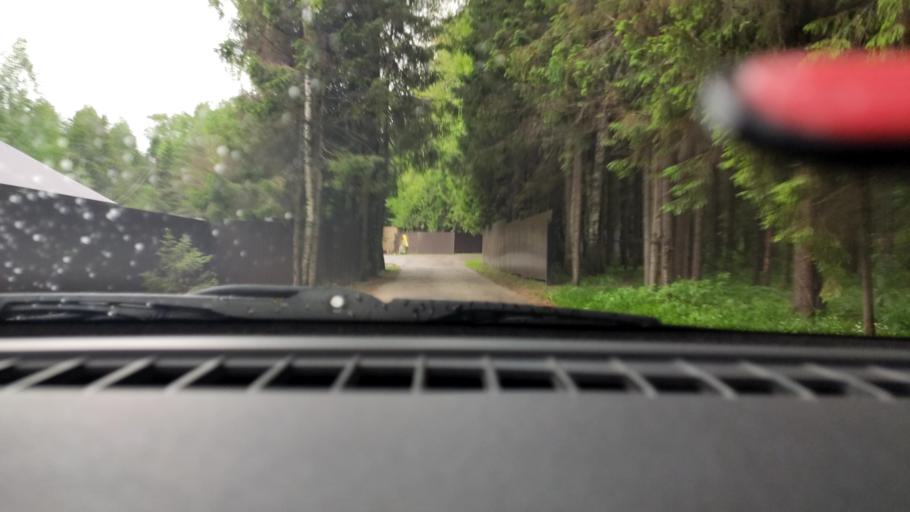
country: RU
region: Perm
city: Karagay
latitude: 58.2373
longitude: 54.8731
